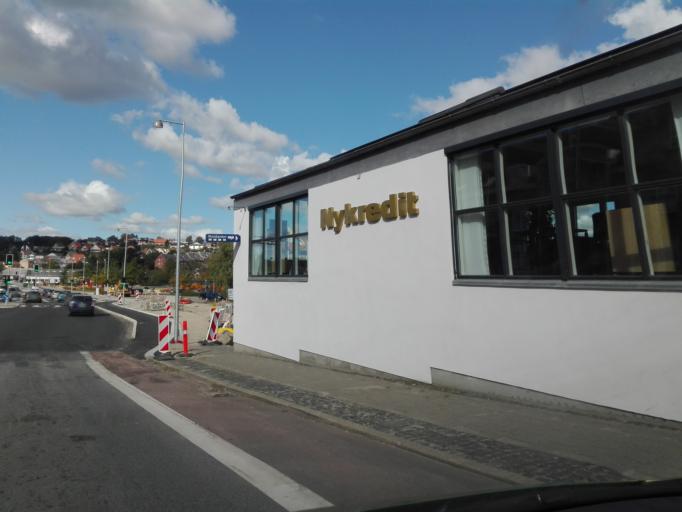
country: DK
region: North Denmark
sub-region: Mariagerfjord Kommune
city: Hobro
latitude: 56.6379
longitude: 9.7987
